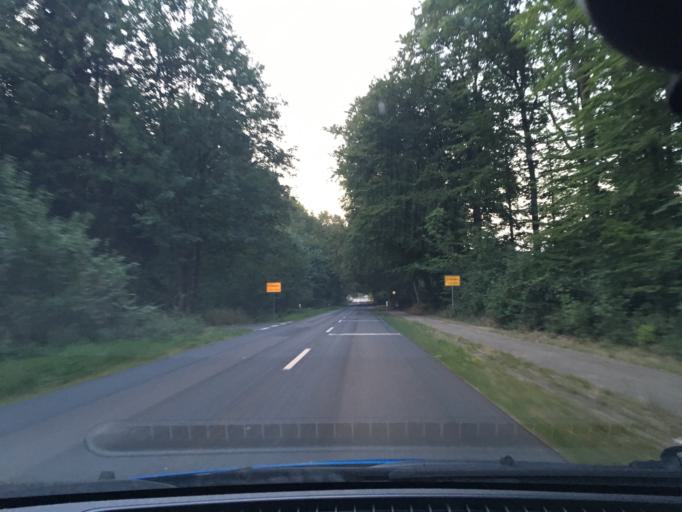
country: DE
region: Lower Saxony
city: Embsen
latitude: 53.1701
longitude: 10.3450
